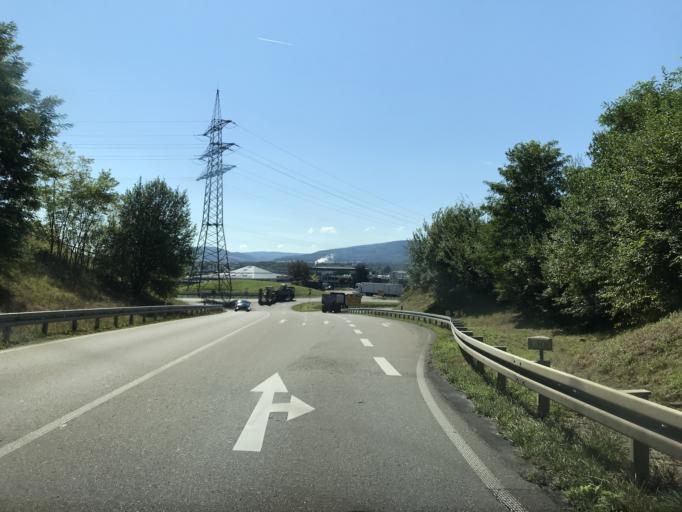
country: DE
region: Baden-Wuerttemberg
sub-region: Freiburg Region
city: Rheinfelden (Baden)
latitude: 47.5781
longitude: 7.7947
